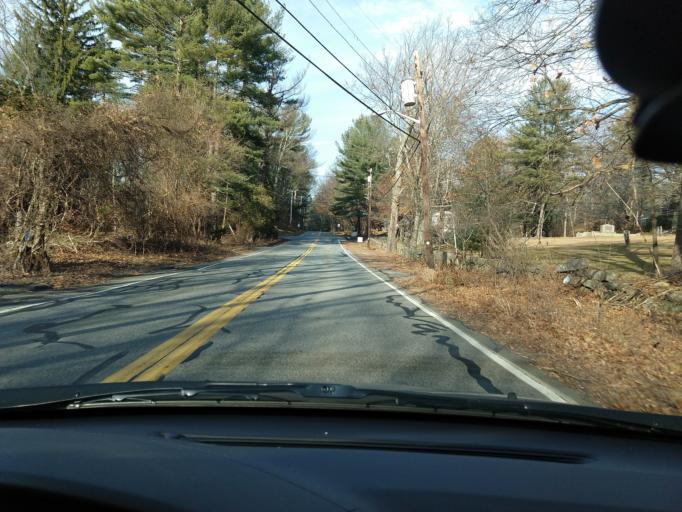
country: US
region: Massachusetts
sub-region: Middlesex County
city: Billerica
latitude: 42.5289
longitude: -71.2934
